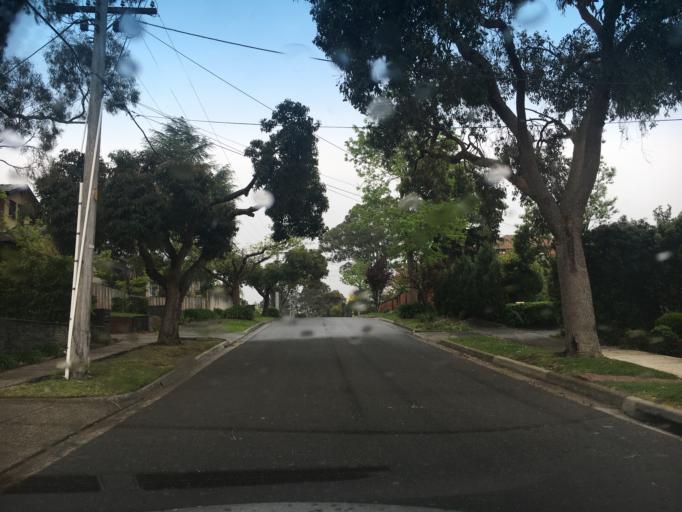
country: AU
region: Victoria
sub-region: Whitehorse
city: Vermont South
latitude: -37.8702
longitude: 145.1665
